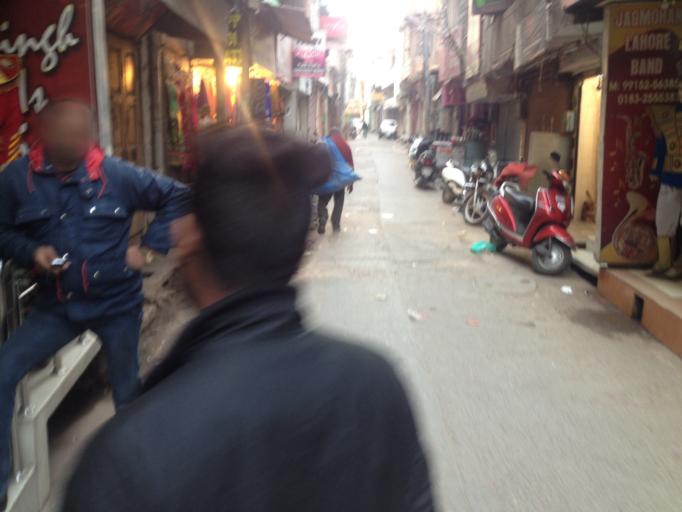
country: IN
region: Punjab
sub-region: Amritsar
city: Amritsar
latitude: 31.6186
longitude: 74.8743
